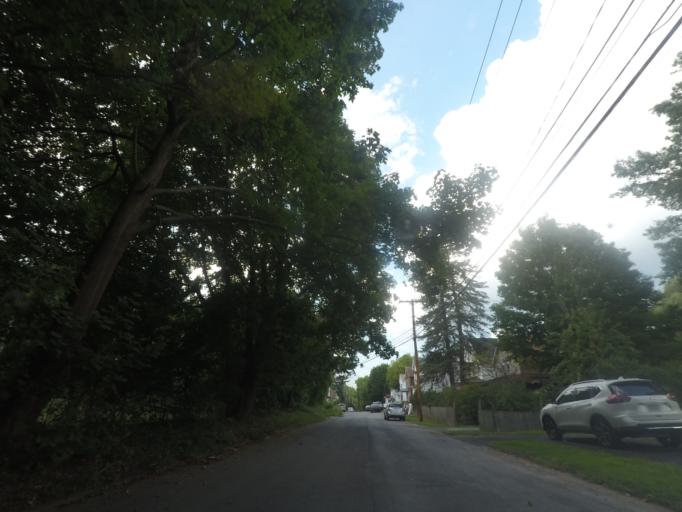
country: US
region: New York
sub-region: Rensselaer County
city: Troy
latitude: 42.7064
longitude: -73.6918
